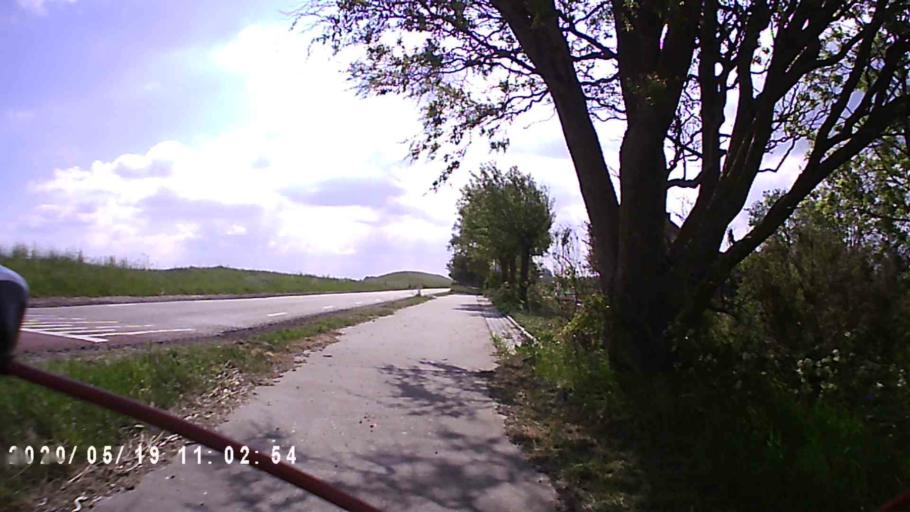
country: NL
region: Groningen
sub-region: Gemeente Zuidhorn
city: Grijpskerk
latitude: 53.2996
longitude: 6.2795
